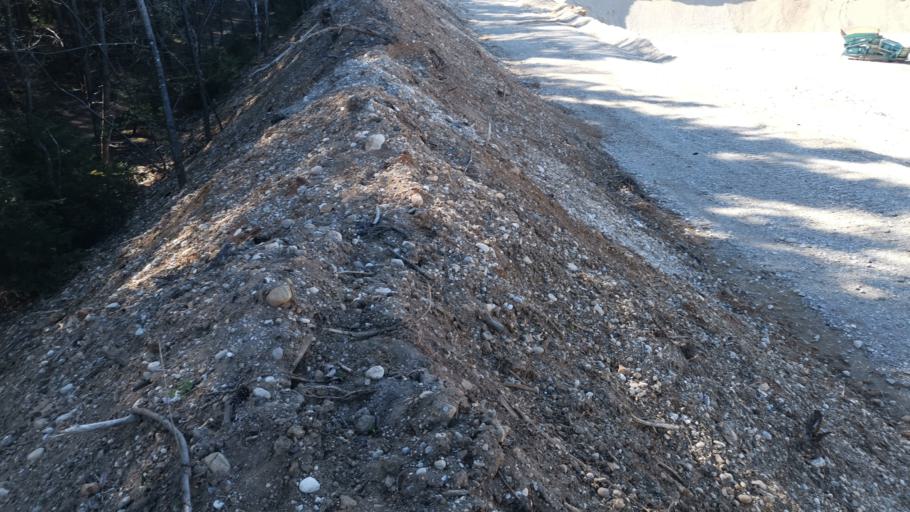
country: DE
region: Bavaria
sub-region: Upper Bavaria
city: Planegg
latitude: 48.0892
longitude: 11.4336
